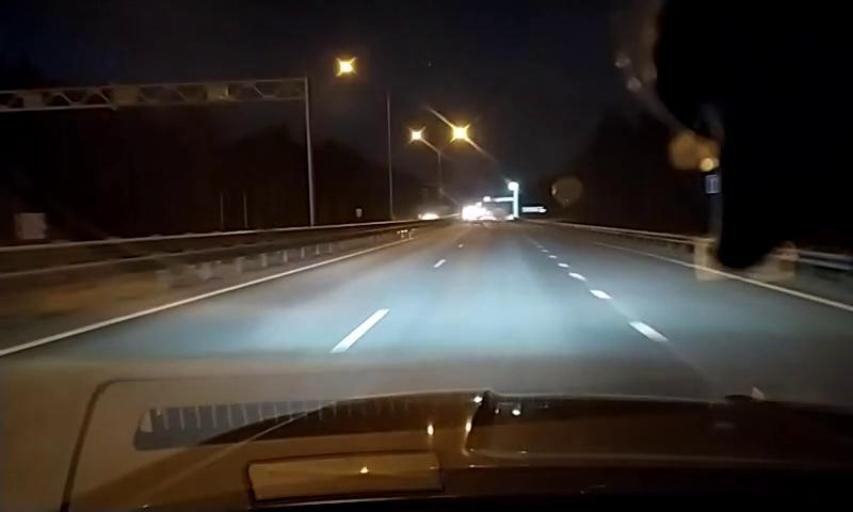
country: RU
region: Leningrad
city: Agalatovo
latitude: 60.2182
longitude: 30.3592
